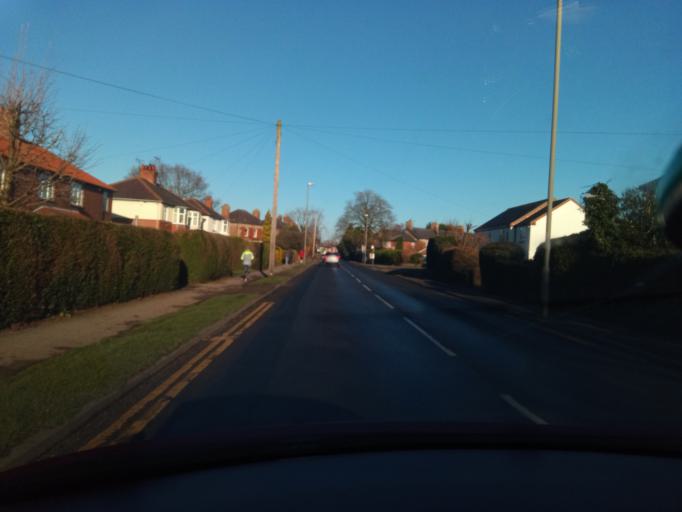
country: GB
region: England
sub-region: North Yorkshire
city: Thirsk
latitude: 54.2274
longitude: -1.3472
